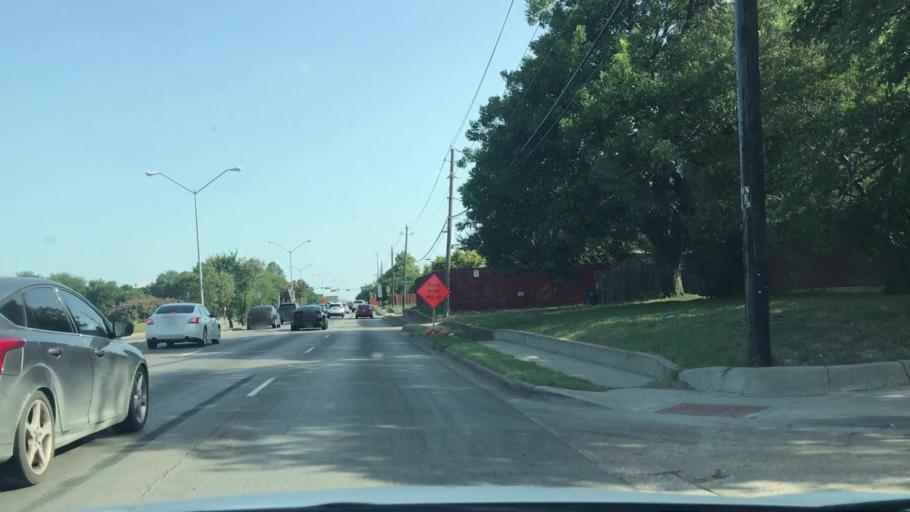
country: US
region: Texas
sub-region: Dallas County
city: Richardson
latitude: 32.9355
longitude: -96.7691
